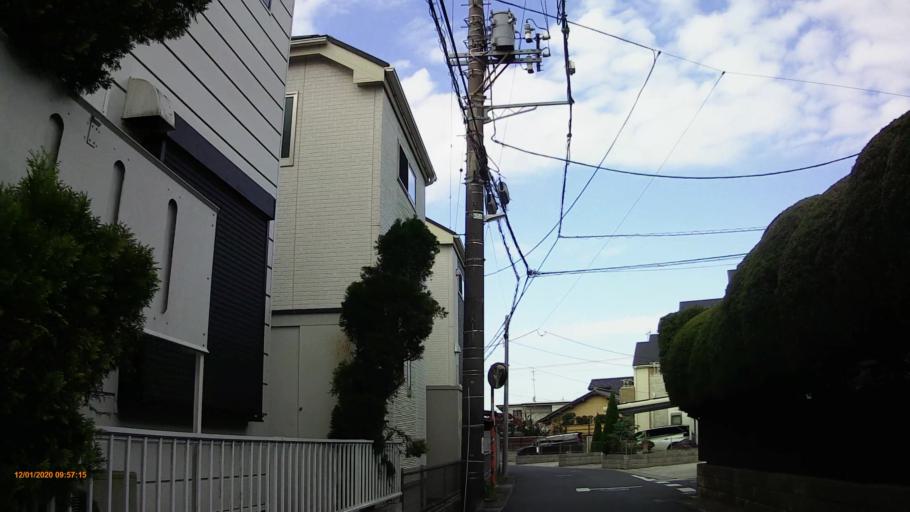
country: JP
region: Chiba
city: Yotsukaido
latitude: 35.6321
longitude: 140.1774
